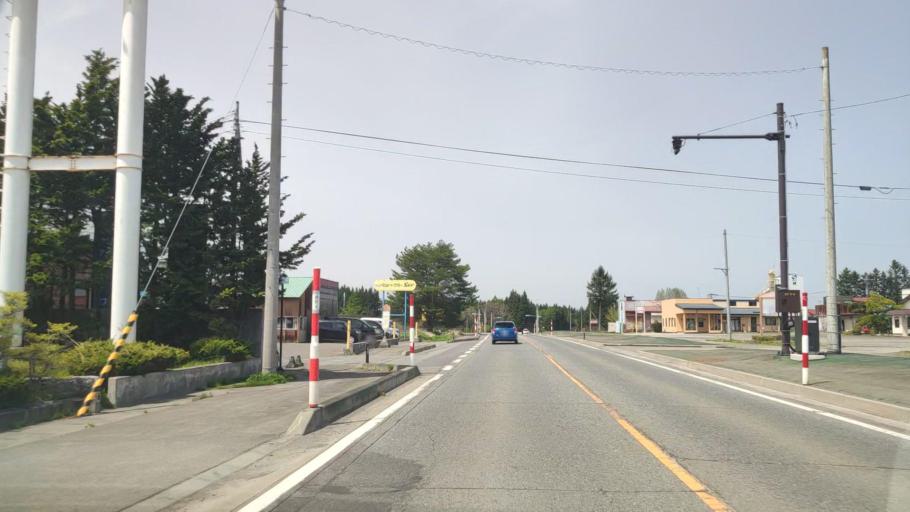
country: JP
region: Aomori
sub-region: Misawa Shi
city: Inuotose
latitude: 40.6762
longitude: 141.1751
